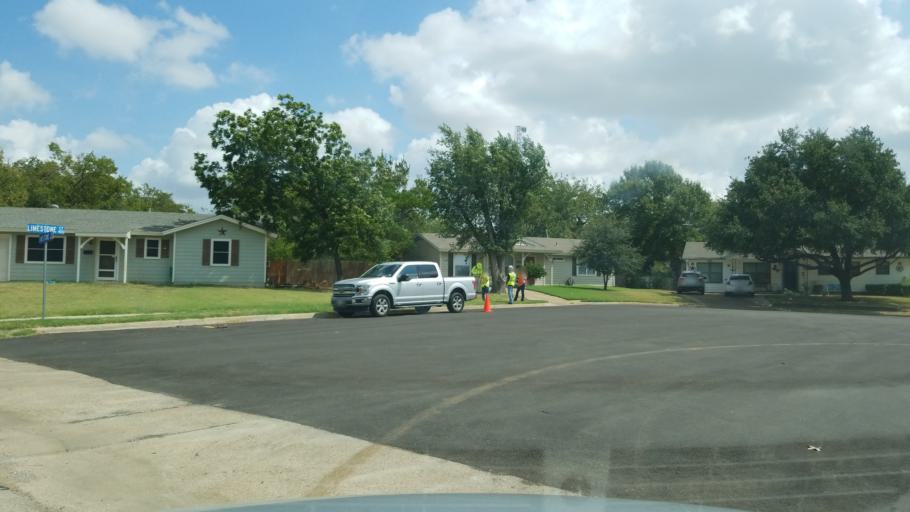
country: US
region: Texas
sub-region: Tarrant County
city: Euless
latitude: 32.8415
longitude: -97.0879
